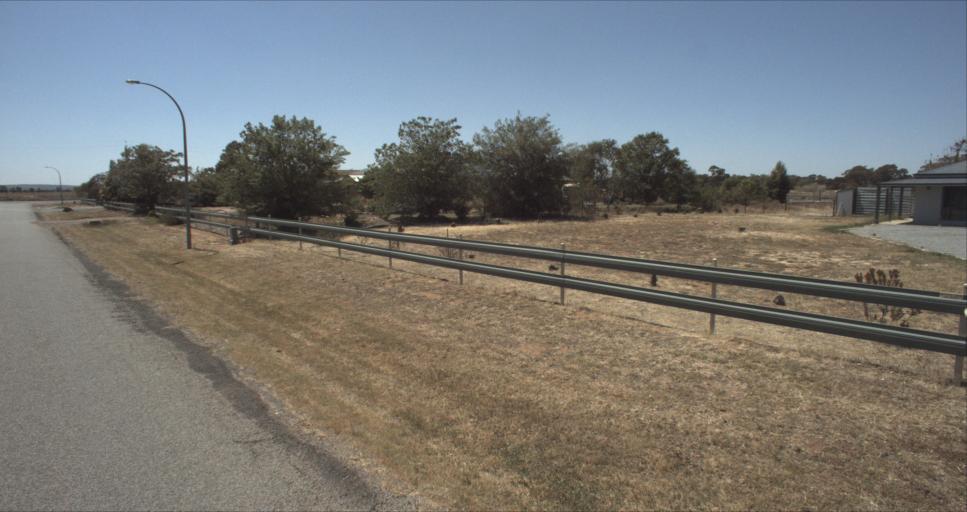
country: AU
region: New South Wales
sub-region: Leeton
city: Leeton
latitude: -34.5291
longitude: 146.3986
